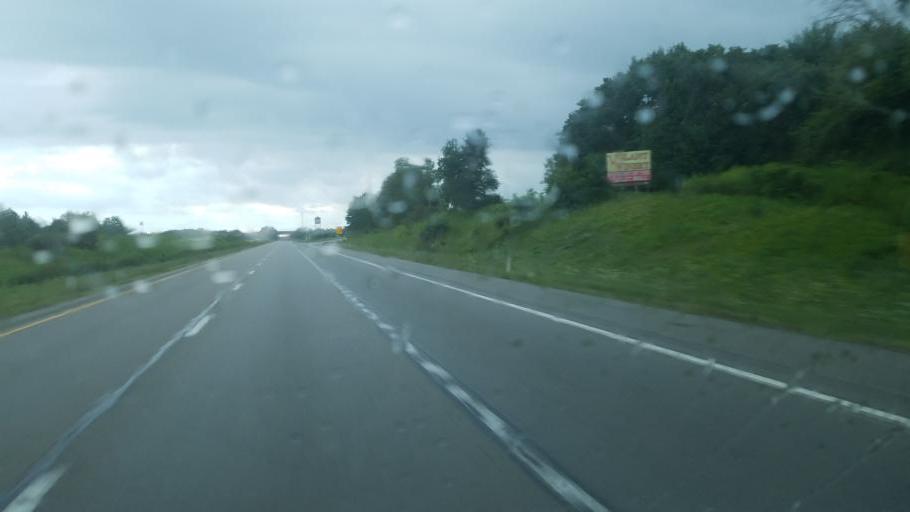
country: US
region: Pennsylvania
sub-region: Mercer County
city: Grove City
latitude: 41.1492
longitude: -80.1560
